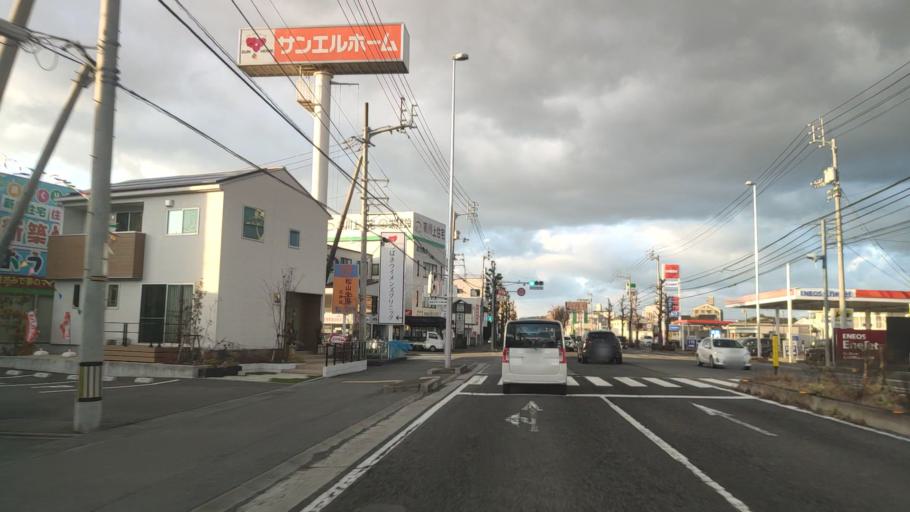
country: JP
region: Ehime
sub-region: Shikoku-chuo Shi
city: Matsuyama
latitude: 33.8064
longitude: 132.7814
